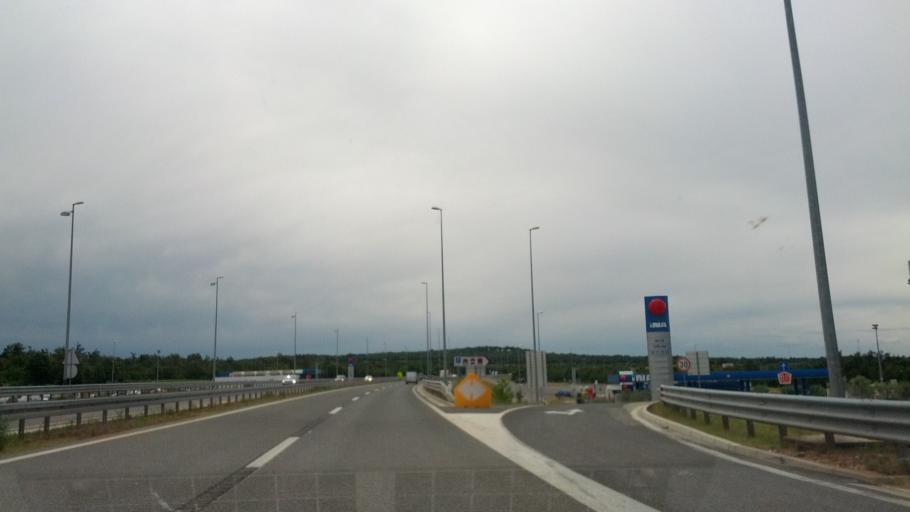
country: HR
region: Istarska
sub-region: Grad Porec
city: Porec
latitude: 45.2399
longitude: 13.7140
